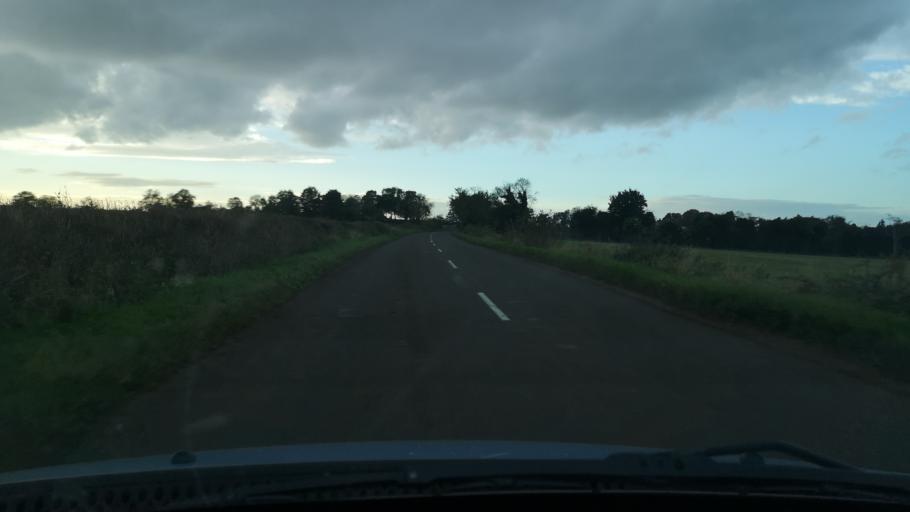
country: GB
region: England
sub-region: Doncaster
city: Norton
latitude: 53.6392
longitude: -1.2135
